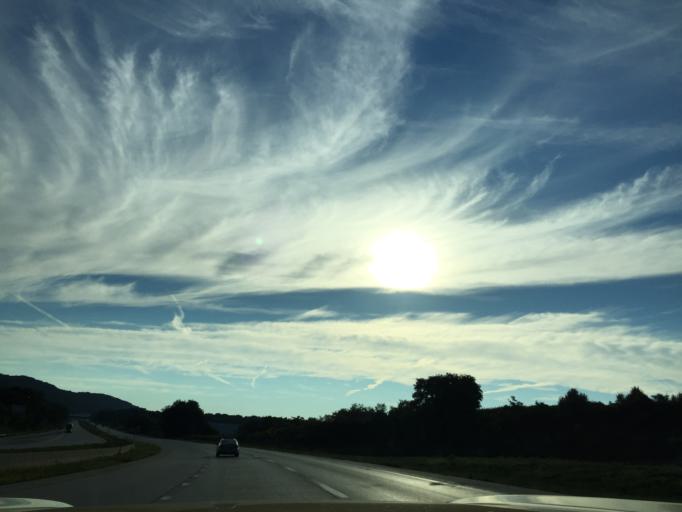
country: US
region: Pennsylvania
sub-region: Lehigh County
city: Fountain Hill
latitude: 40.5548
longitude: -75.4292
